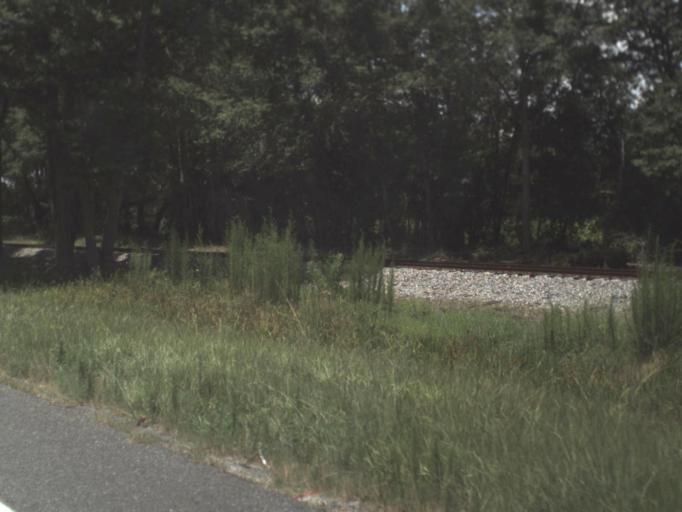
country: US
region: Florida
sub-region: Columbia County
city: Five Points
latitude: 30.2652
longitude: -82.6887
